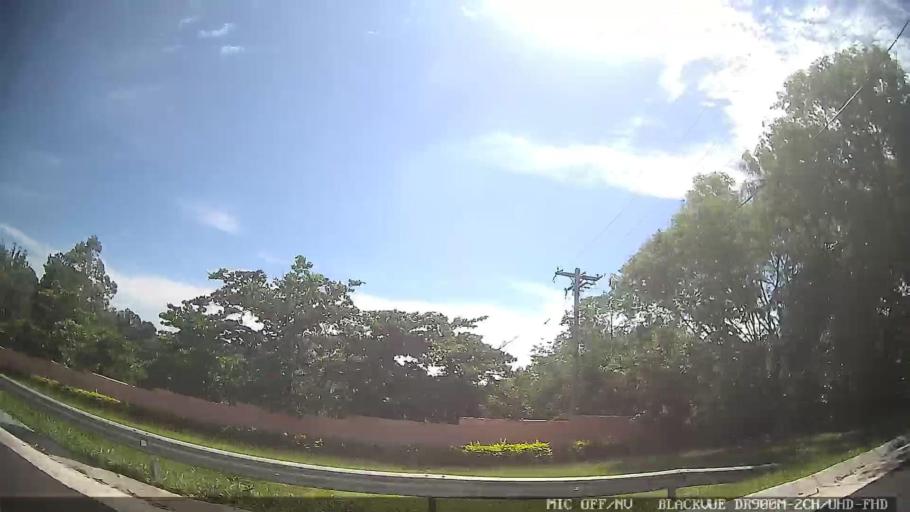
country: BR
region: Sao Paulo
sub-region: Tiete
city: Tiete
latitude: -23.1657
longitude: -47.6458
